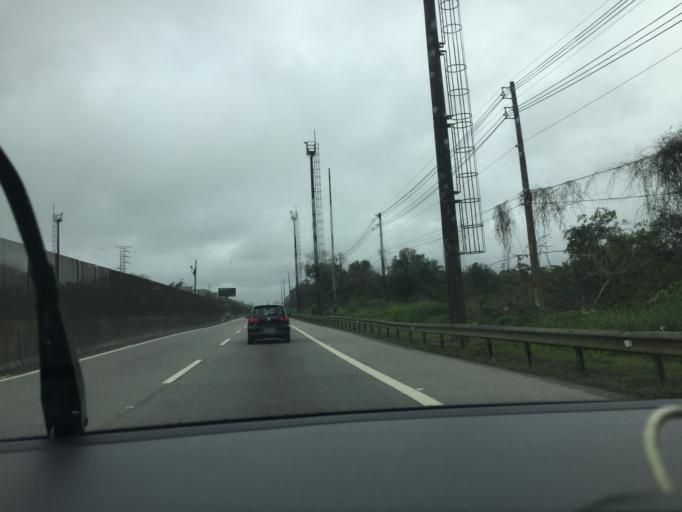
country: BR
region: Sao Paulo
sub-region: Santos
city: Santos
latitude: -23.8958
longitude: -46.3020
